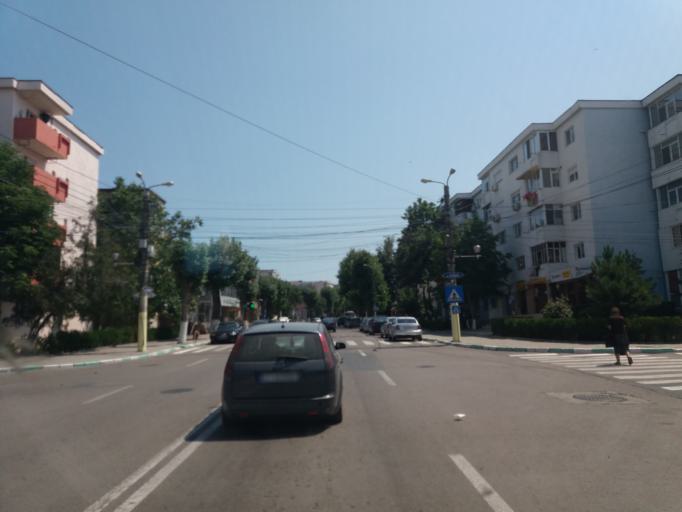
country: RO
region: Constanta
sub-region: Comuna Navodari
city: Navodari
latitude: 44.3200
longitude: 28.6089
